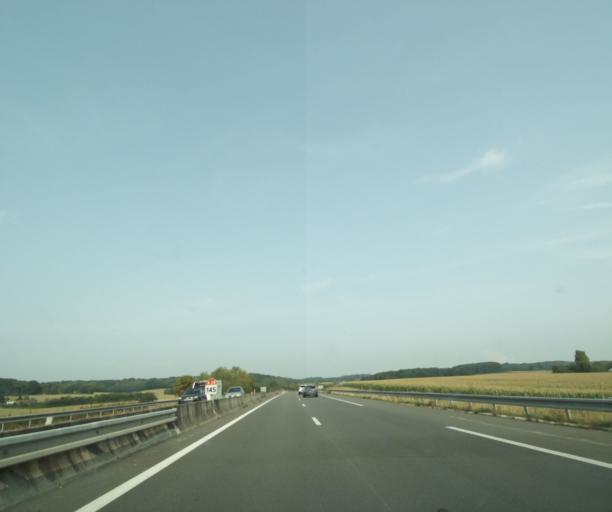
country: FR
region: Pays de la Loire
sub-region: Departement de la Sarthe
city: Champfleur
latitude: 48.3266
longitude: 0.1171
